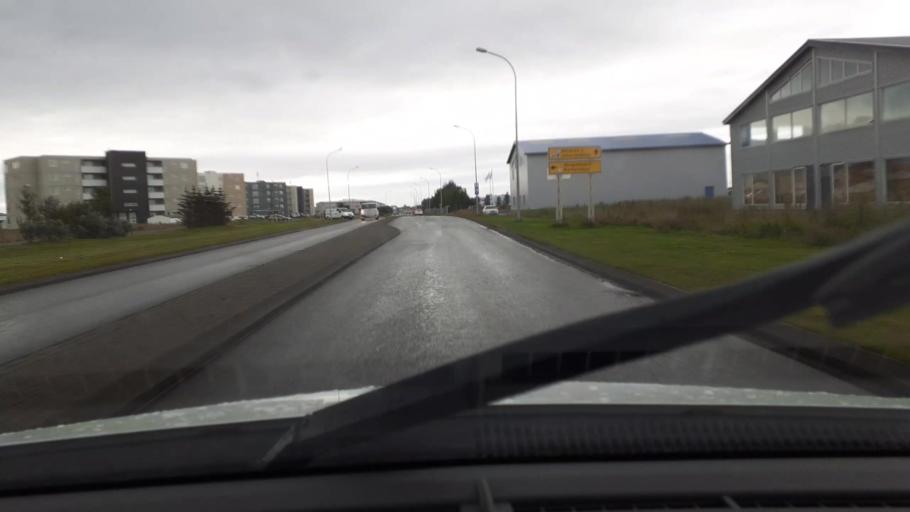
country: IS
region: West
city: Akranes
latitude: 64.3260
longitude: -22.0557
